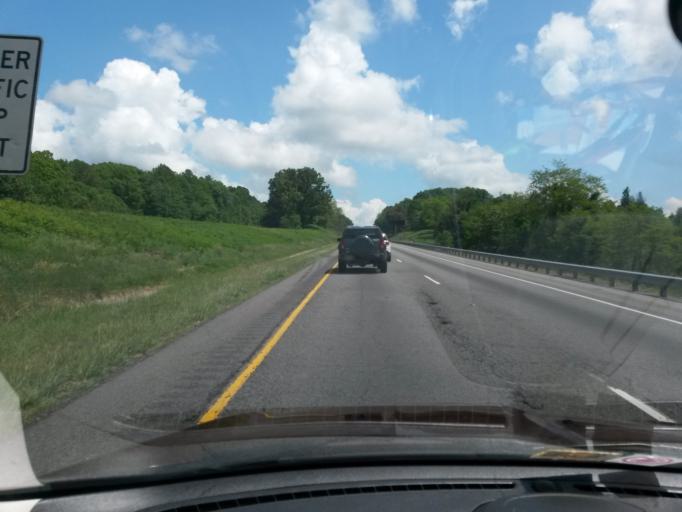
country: US
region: Virginia
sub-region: Carroll County
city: Woodlawn
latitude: 36.8037
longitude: -80.8499
